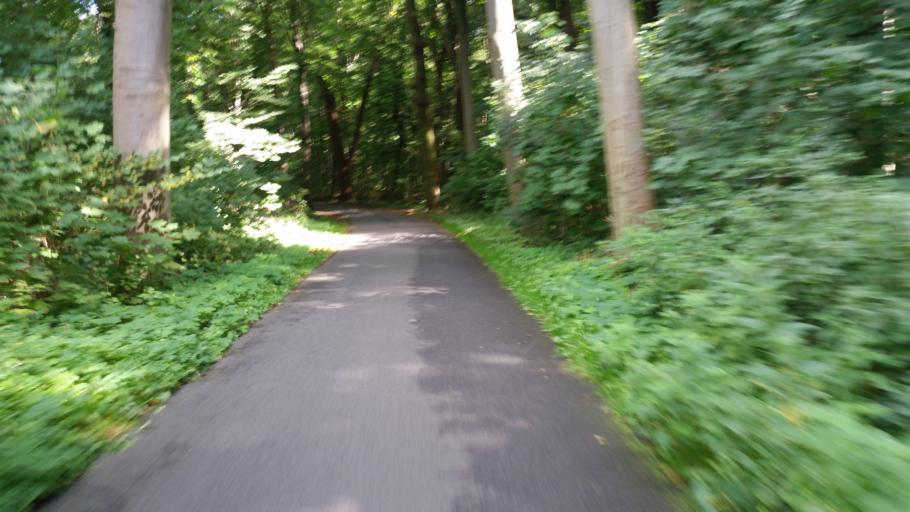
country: DE
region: Lower Saxony
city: Hannover
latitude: 52.3914
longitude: 9.7596
